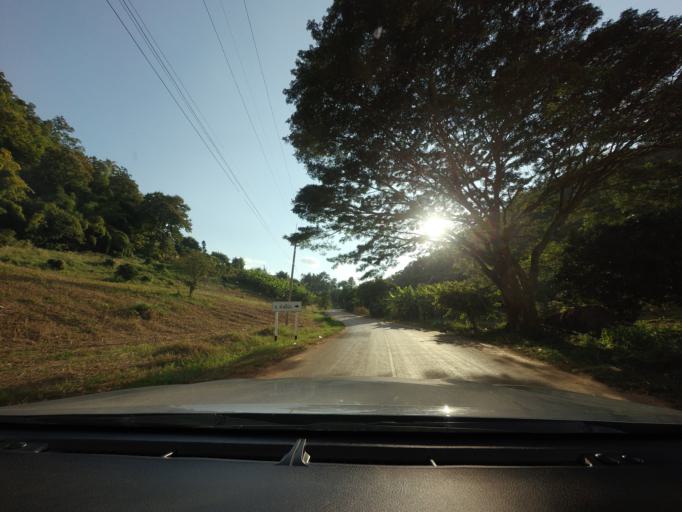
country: TH
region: Chiang Mai
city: Chai Prakan
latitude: 19.6204
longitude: 99.1658
